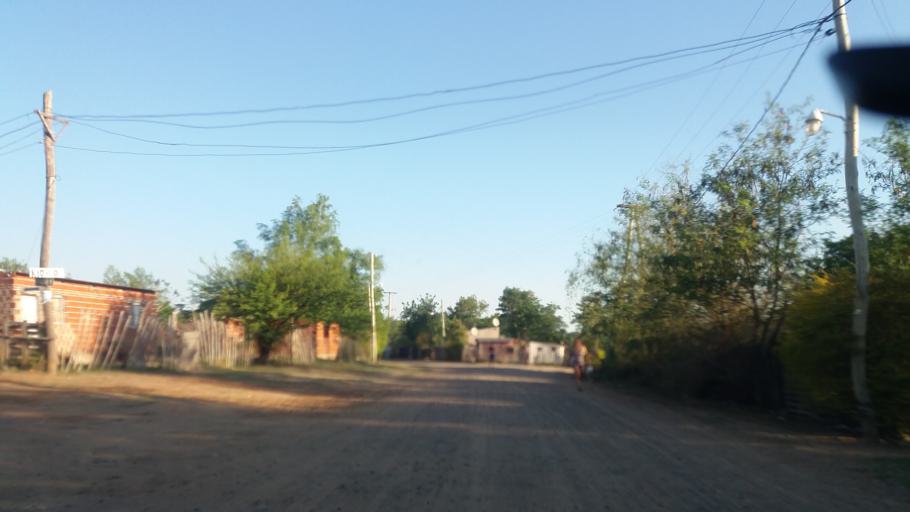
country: AR
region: Corrientes
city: Corrientes
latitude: -27.5185
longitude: -58.8296
